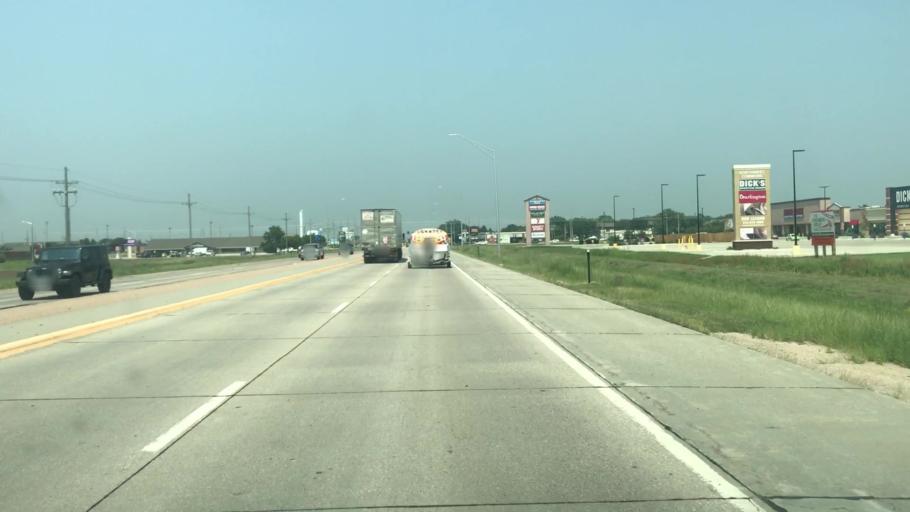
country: US
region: Nebraska
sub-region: Hall County
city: Grand Island
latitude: 40.9420
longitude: -98.3835
